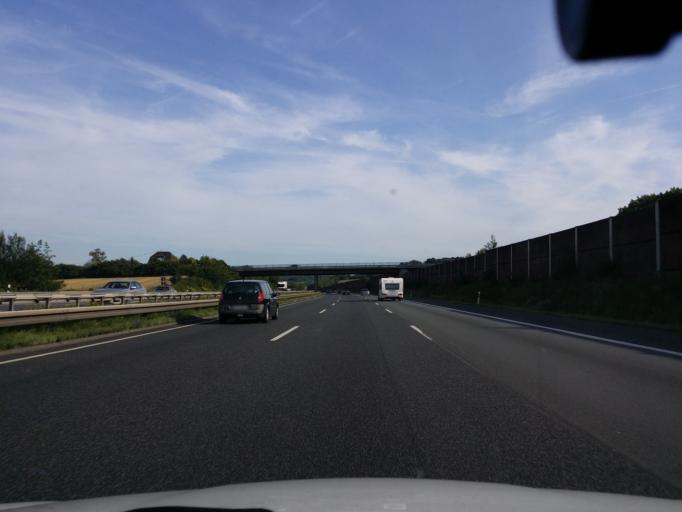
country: DE
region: North Rhine-Westphalia
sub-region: Regierungsbezirk Koln
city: Konigswinter
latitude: 50.7076
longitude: 7.2483
